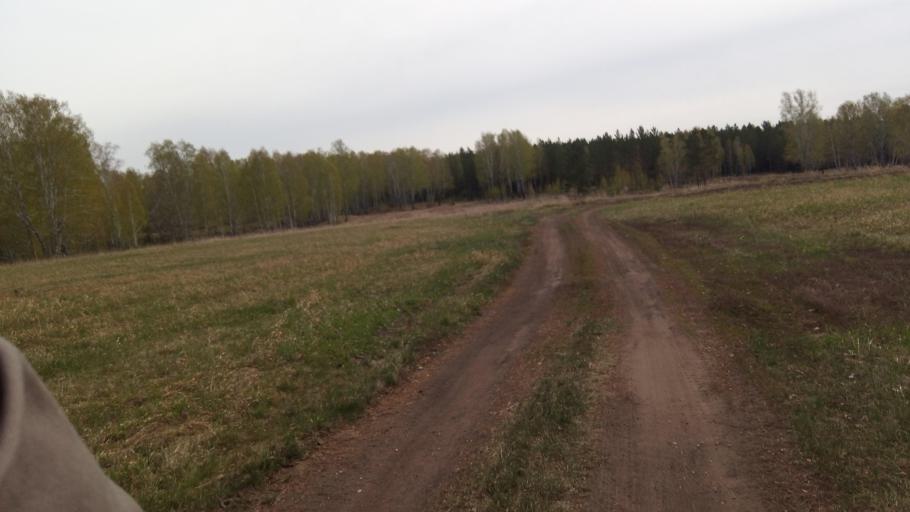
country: RU
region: Chelyabinsk
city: Timiryazevskiy
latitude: 55.0231
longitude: 60.8509
